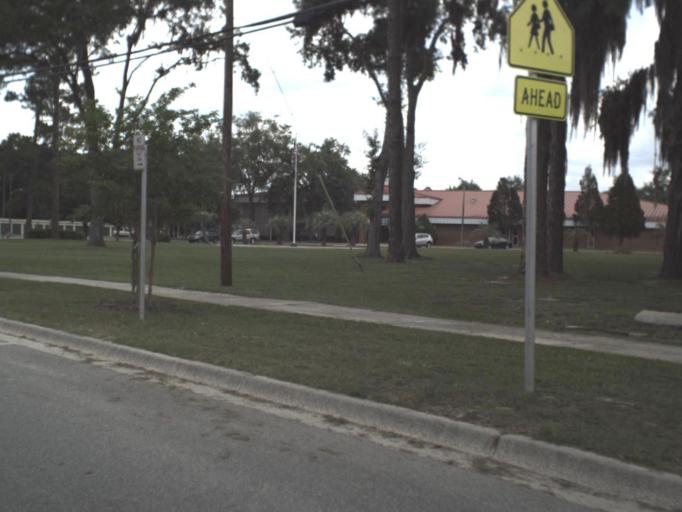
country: US
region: Florida
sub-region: Hamilton County
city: Jasper
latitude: 30.5234
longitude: -82.9587
